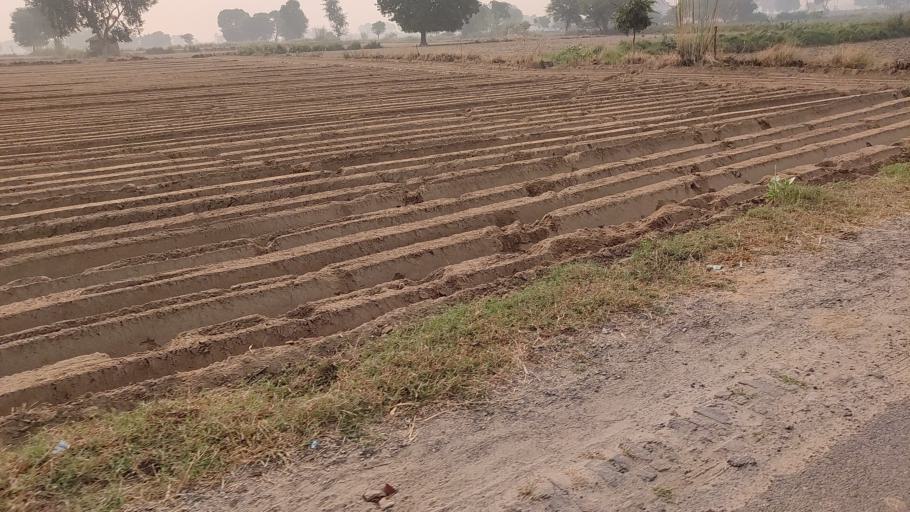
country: IN
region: Uttar Pradesh
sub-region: Mathura
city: Vrindavan
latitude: 27.5464
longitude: 77.7115
